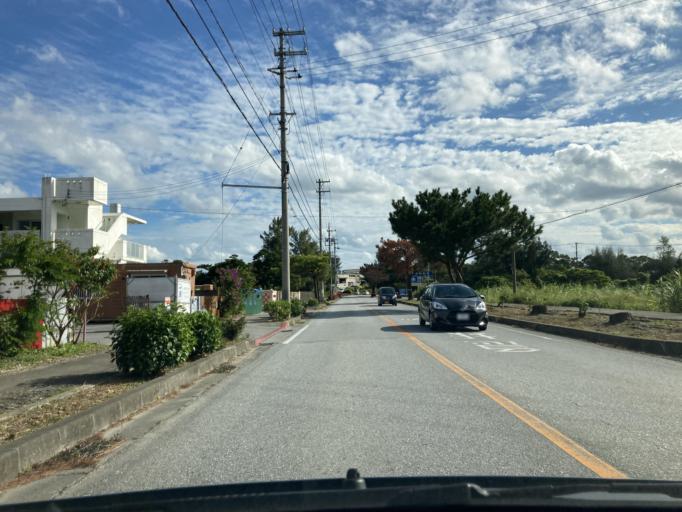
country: JP
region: Okinawa
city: Ishikawa
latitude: 26.4308
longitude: 127.8070
